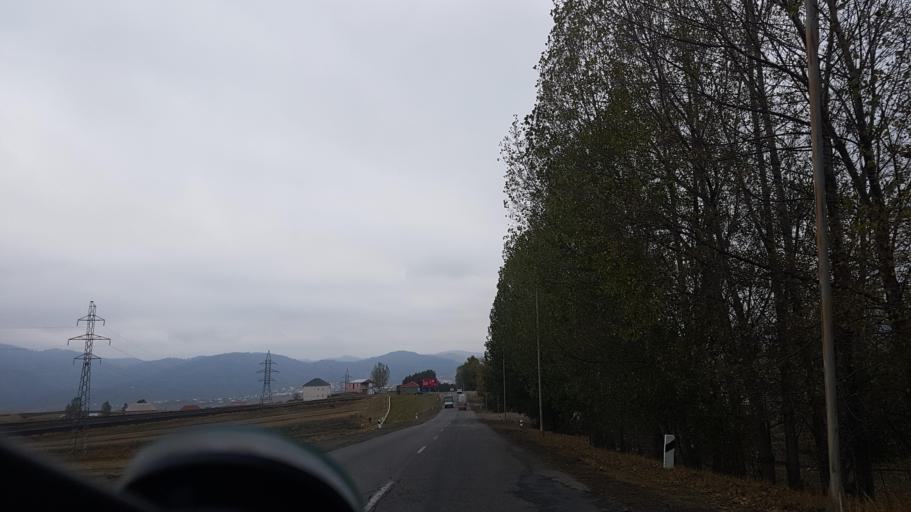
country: AZ
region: Gadabay Rayon
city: Ariqdam
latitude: 40.6093
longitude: 45.8127
